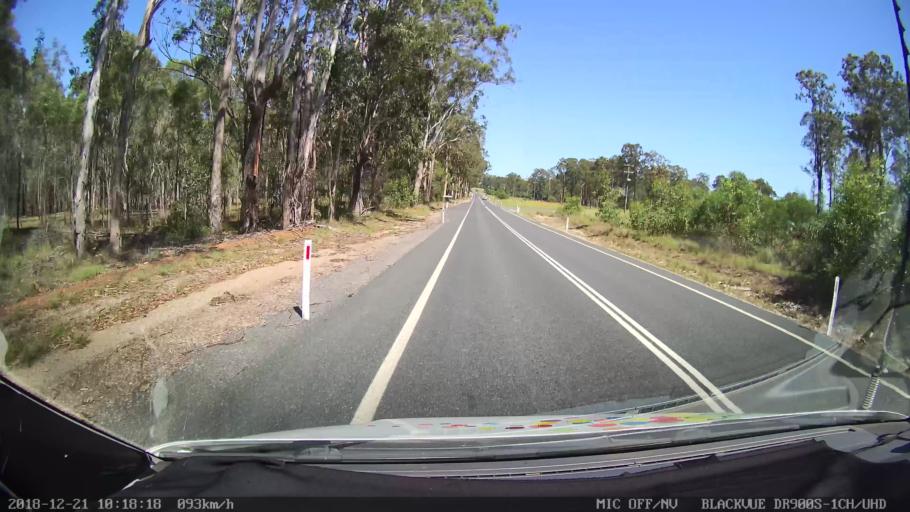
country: AU
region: New South Wales
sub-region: Clarence Valley
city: South Grafton
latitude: -29.6843
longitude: 152.8581
